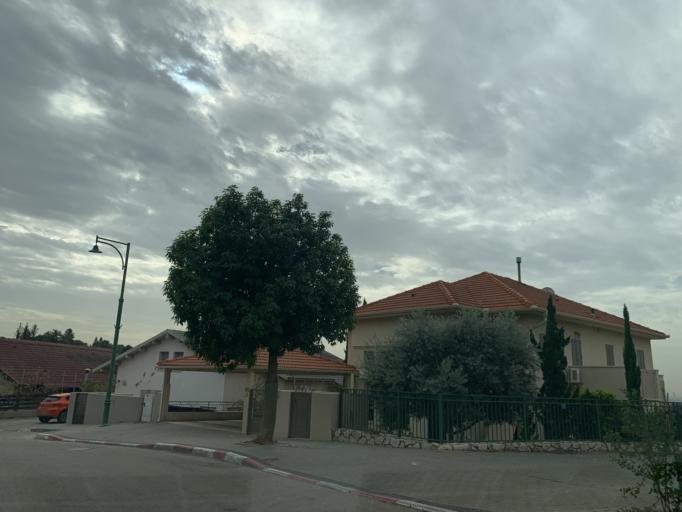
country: IL
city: Nirit
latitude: 32.1497
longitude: 34.9857
